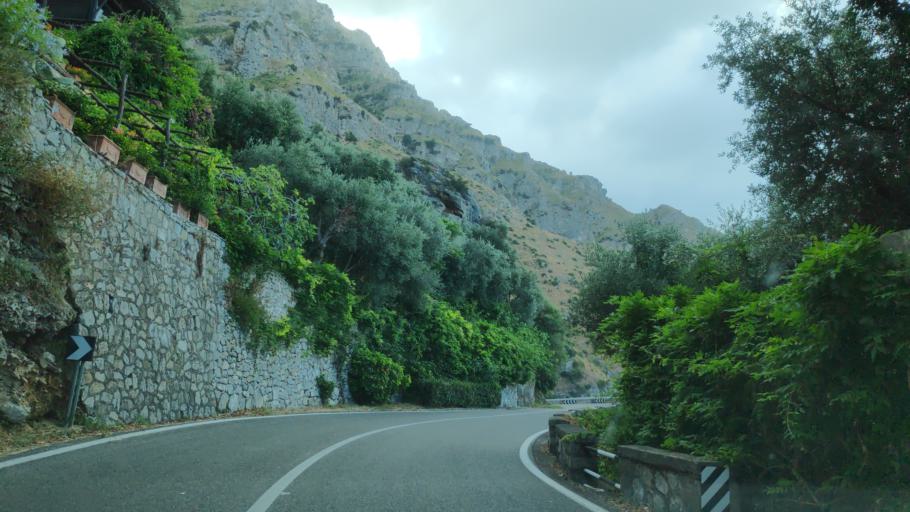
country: IT
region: Campania
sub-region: Provincia di Napoli
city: Arola-Preazzano
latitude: 40.6210
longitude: 14.4521
